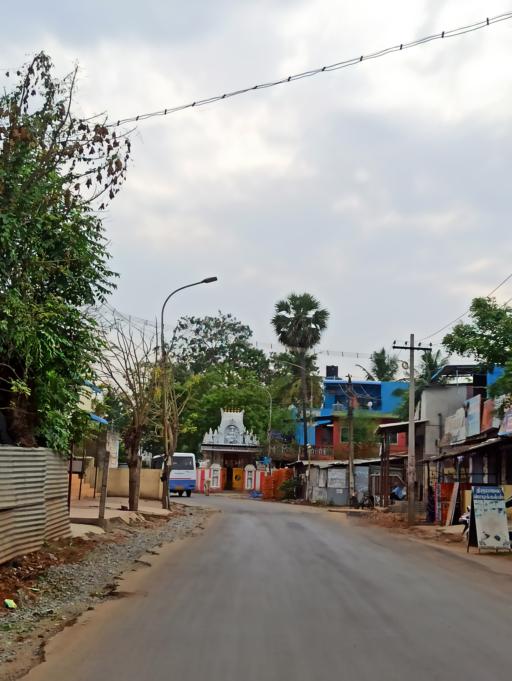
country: IN
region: Tamil Nadu
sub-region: Thiruvallur
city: Chinnasekkadu
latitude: 13.1673
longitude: 80.2417
